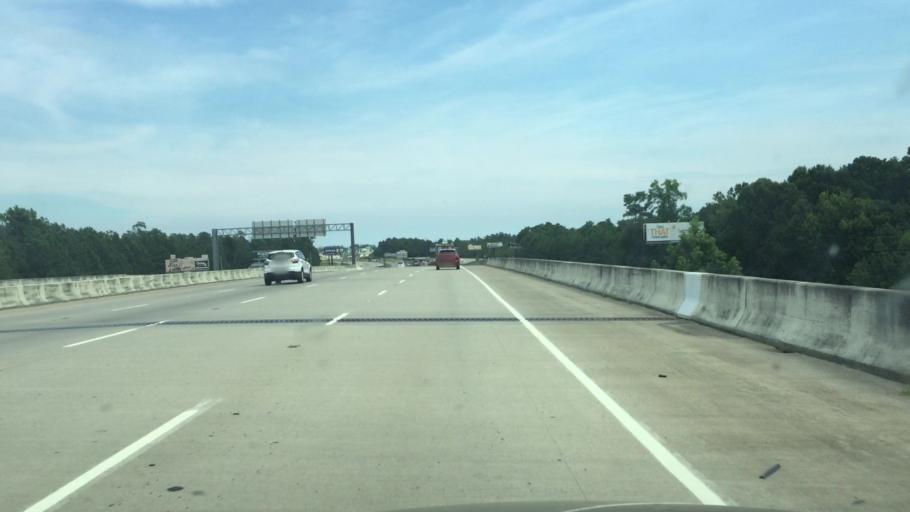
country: US
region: South Carolina
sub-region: Horry County
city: Forestbrook
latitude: 33.7320
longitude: -78.9443
